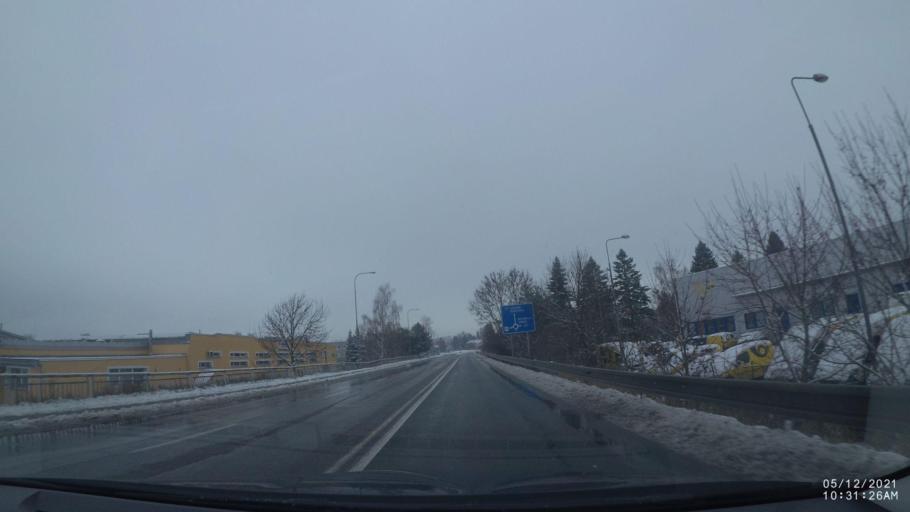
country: CZ
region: Kralovehradecky
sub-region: Okres Rychnov nad Kneznou
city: Rychnov nad Kneznou
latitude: 50.1524
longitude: 16.2818
